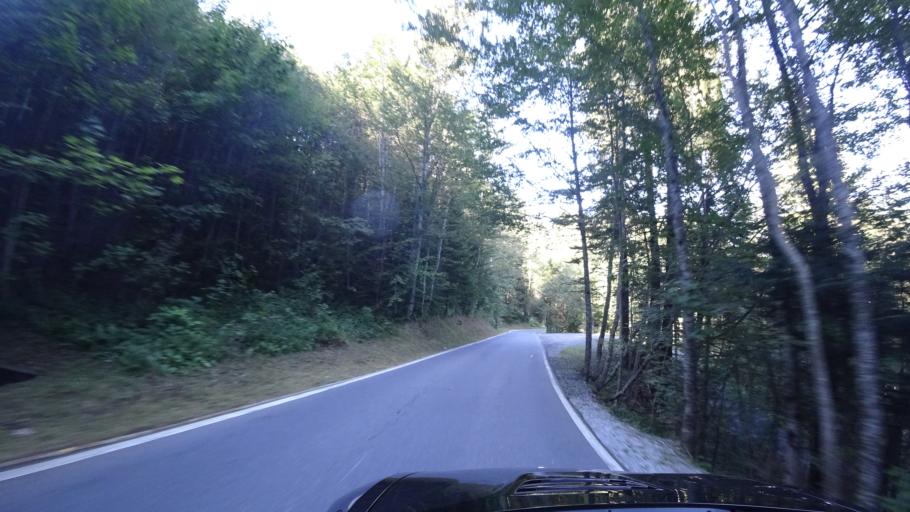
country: CH
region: Obwalden
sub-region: Obwalden
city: Giswil
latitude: 46.8323
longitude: 8.1341
